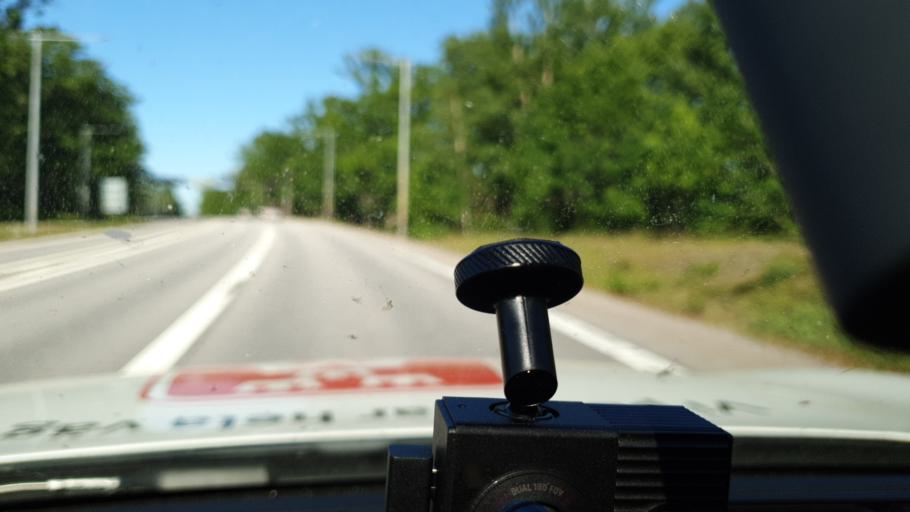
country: SE
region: Kalmar
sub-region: Vasterviks Kommun
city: Vaestervik
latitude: 57.7639
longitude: 16.5606
